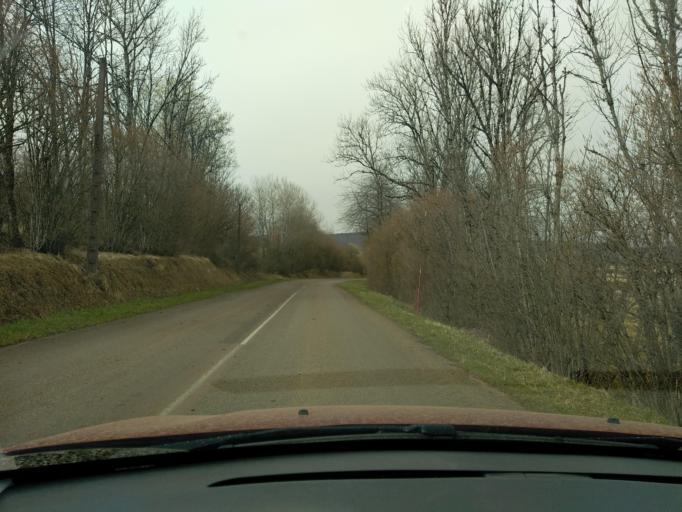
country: FR
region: Franche-Comte
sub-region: Departement du Jura
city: Clairvaux-les-Lacs
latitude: 46.6653
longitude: 5.7712
